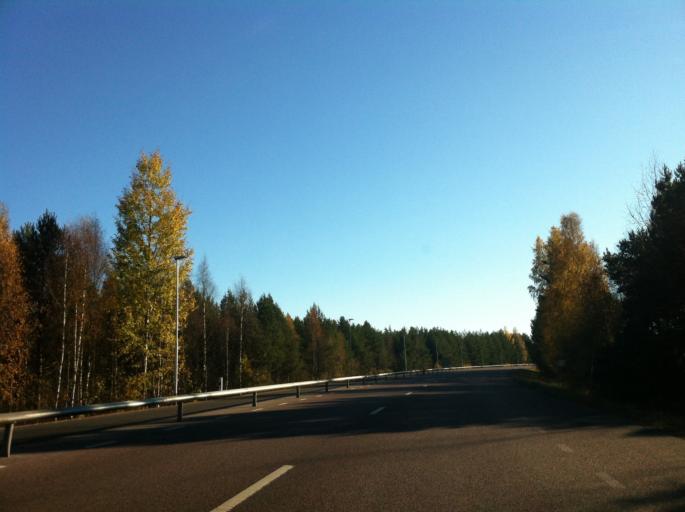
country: SE
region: Dalarna
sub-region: Mora Kommun
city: Mora
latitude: 61.0236
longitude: 14.5349
